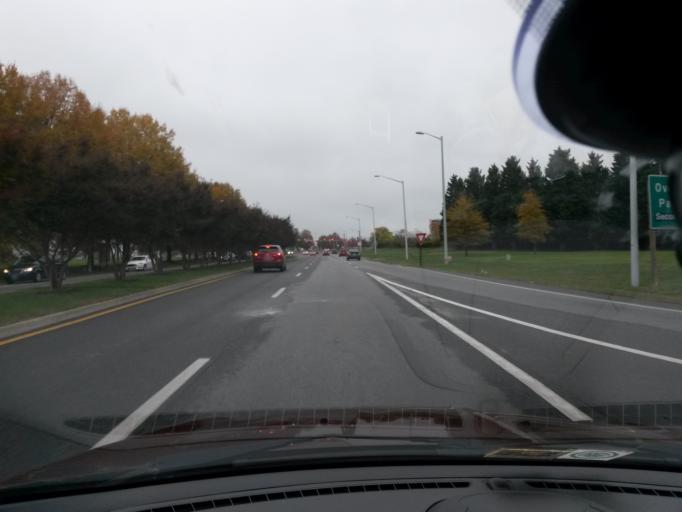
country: US
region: Virginia
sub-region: Roanoke County
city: Hollins
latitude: 37.3158
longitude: -79.9671
